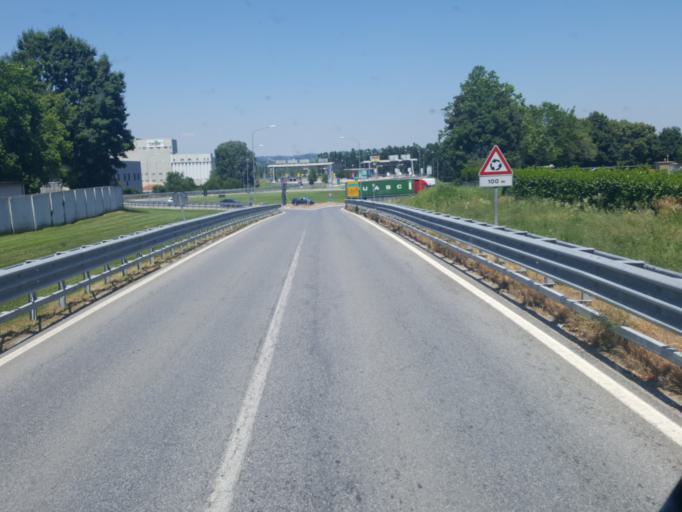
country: IT
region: Piedmont
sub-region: Provincia di Cuneo
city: Cherasco
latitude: 44.6498
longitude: 7.8701
